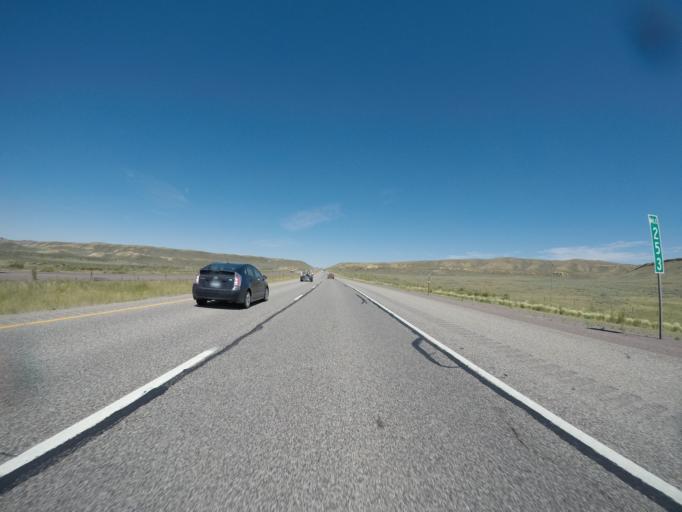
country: US
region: Wyoming
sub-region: Carbon County
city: Saratoga
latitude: 41.7464
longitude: -106.4982
